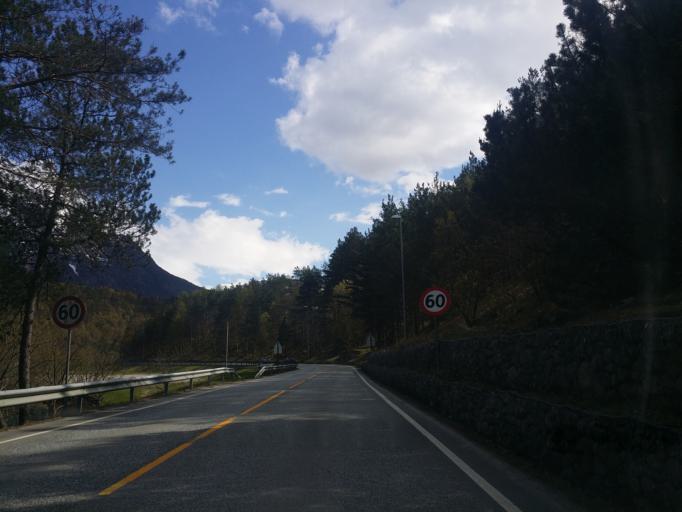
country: NO
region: Hordaland
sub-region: Eidfjord
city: Eidfjord
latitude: 60.4650
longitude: 7.0723
